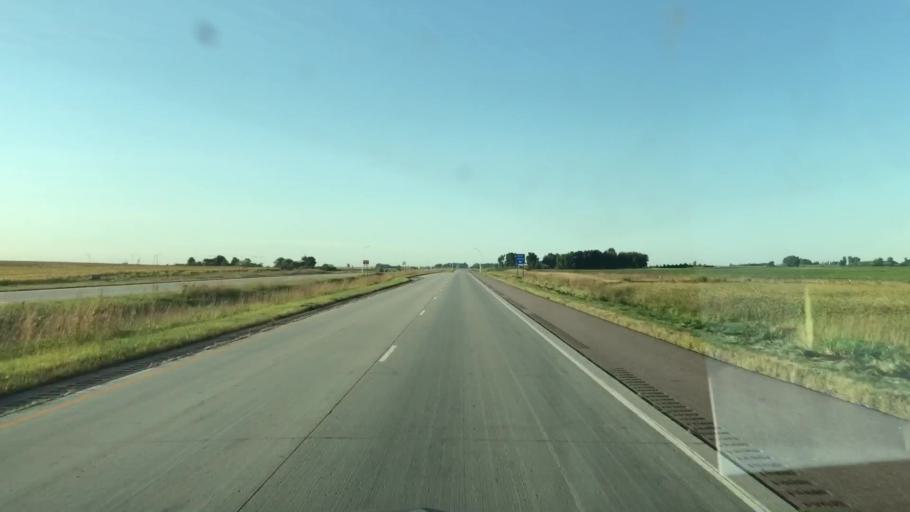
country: US
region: Minnesota
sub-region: Nobles County
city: Worthington
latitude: 43.5722
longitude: -95.6536
